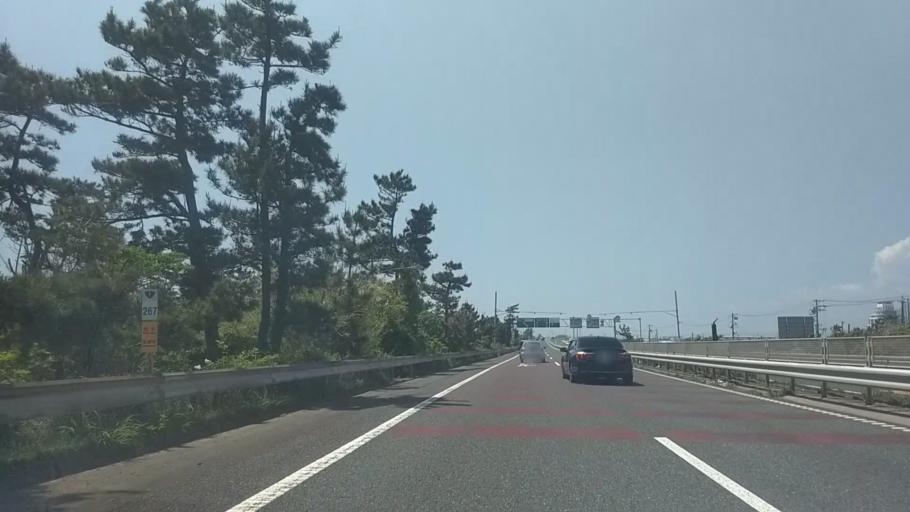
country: JP
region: Shizuoka
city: Hamamatsu
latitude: 34.6751
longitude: 137.6553
